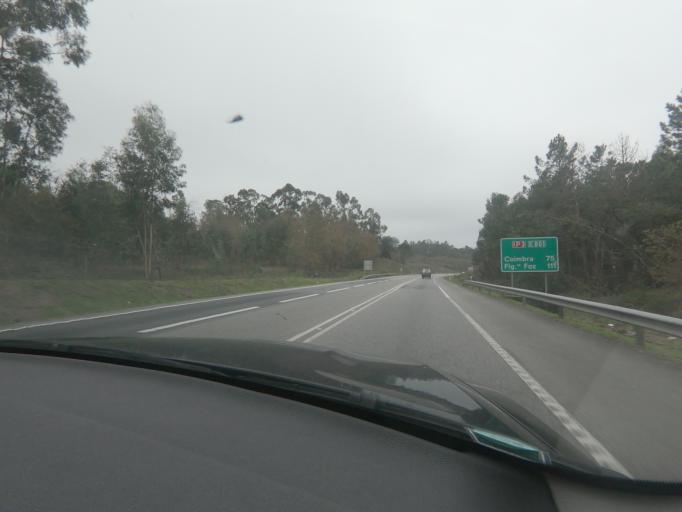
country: PT
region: Viseu
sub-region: Concelho de Tondela
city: Tondela
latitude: 40.5829
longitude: -8.0183
